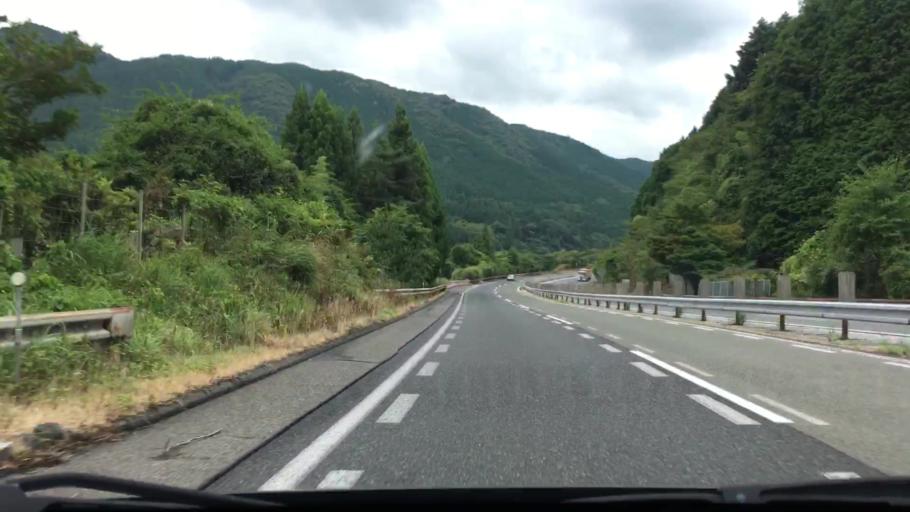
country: JP
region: Okayama
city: Niimi
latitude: 34.9865
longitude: 133.3819
